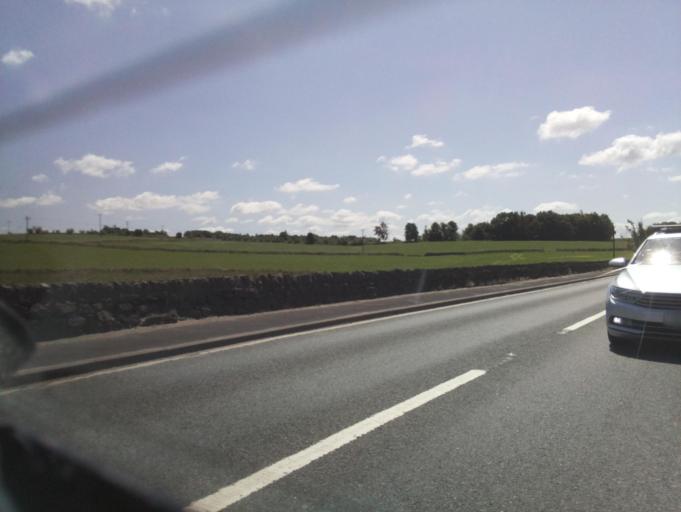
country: GB
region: England
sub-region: Derbyshire
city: Chapel en le Frith
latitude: 53.2939
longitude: -1.8887
